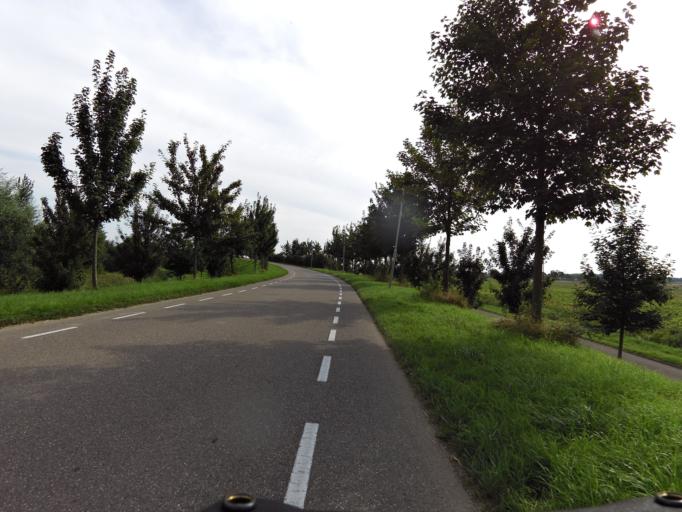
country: NL
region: South Holland
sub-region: Gemeente Zwijndrecht
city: Heerjansdam
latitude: 51.7949
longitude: 4.5850
